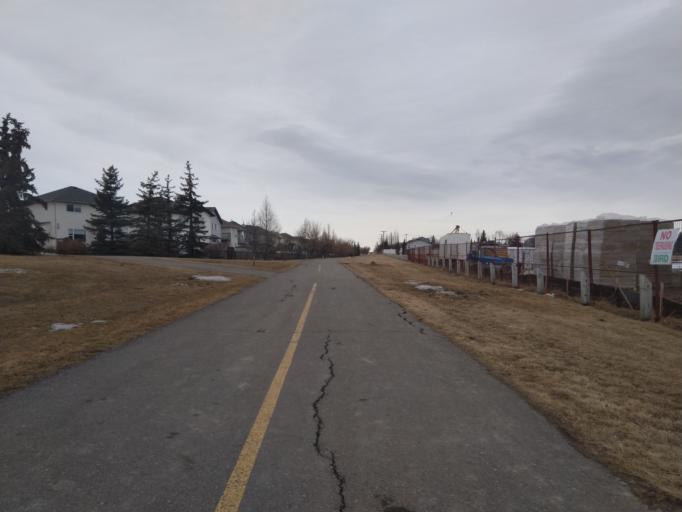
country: CA
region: Alberta
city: Calgary
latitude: 51.1574
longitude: -114.0480
